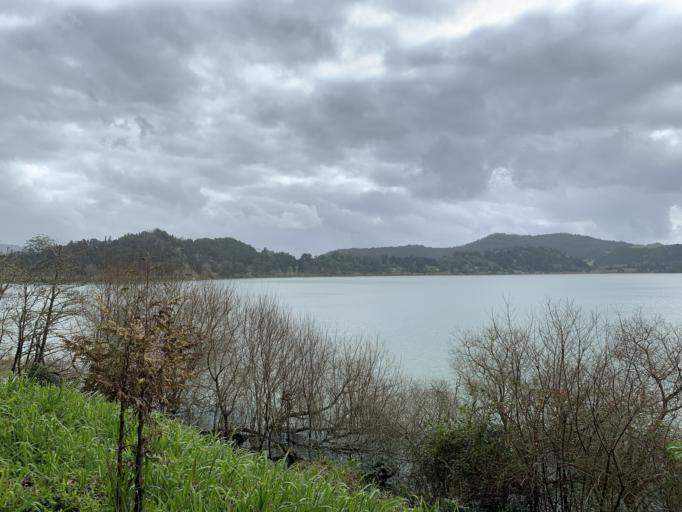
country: PT
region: Azores
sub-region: Povoacao
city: Furnas
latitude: 37.7636
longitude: -25.3372
